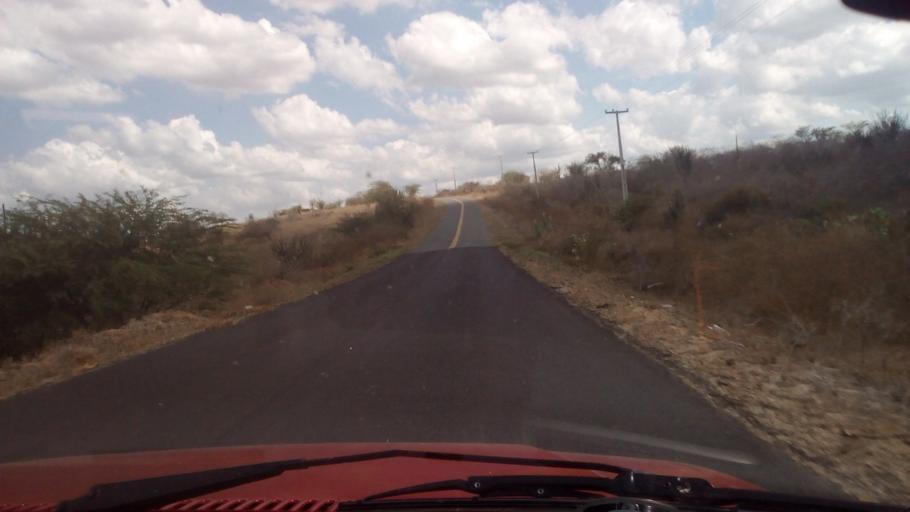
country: BR
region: Paraiba
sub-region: Cacimba De Dentro
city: Cacimba de Dentro
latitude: -6.6953
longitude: -35.7385
